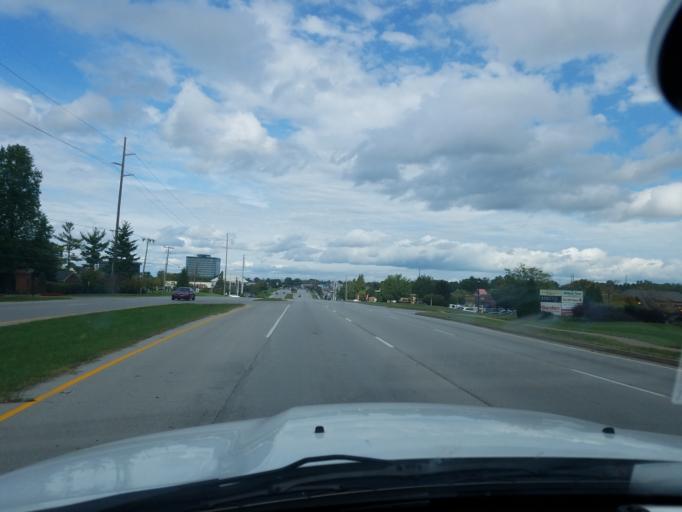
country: US
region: Kentucky
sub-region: Jefferson County
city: Hurstbourne
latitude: 38.2378
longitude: -85.5769
